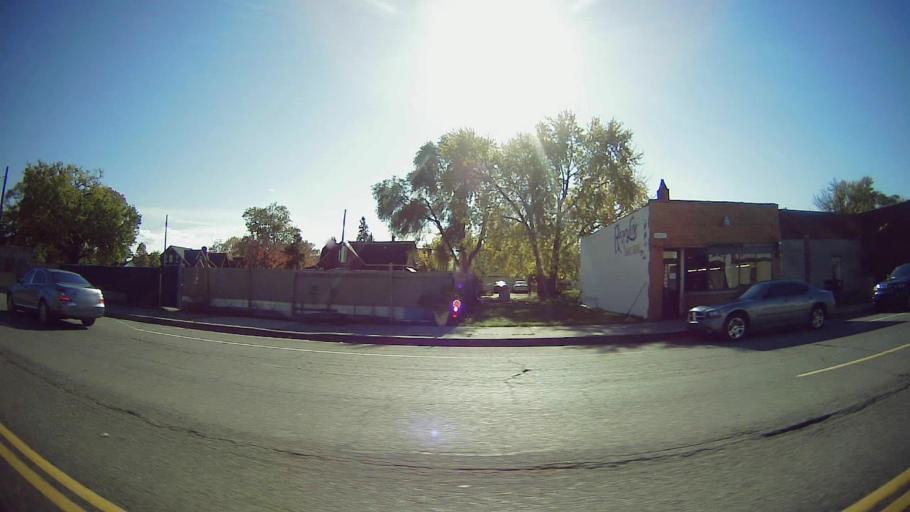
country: US
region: Michigan
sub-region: Wayne County
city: Dearborn
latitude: 42.3661
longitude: -83.1638
